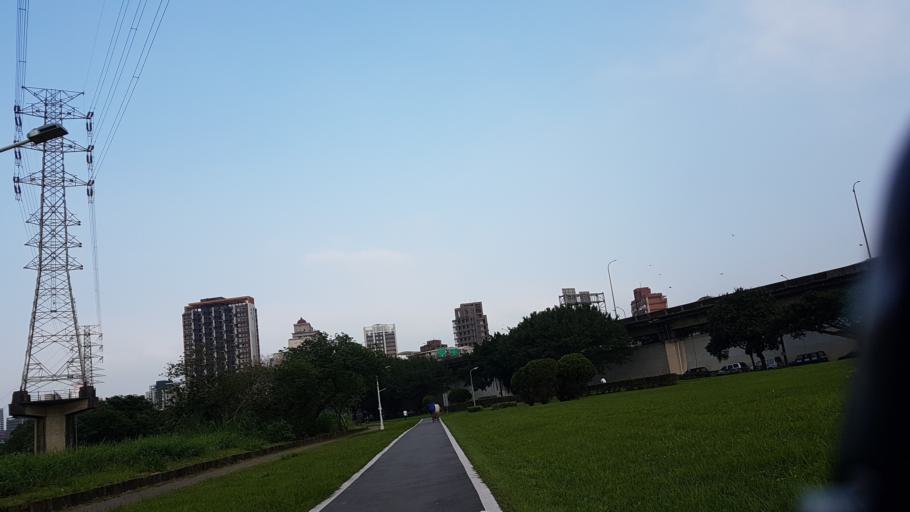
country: TW
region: Taipei
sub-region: Taipei
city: Banqiao
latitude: 25.0384
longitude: 121.4929
